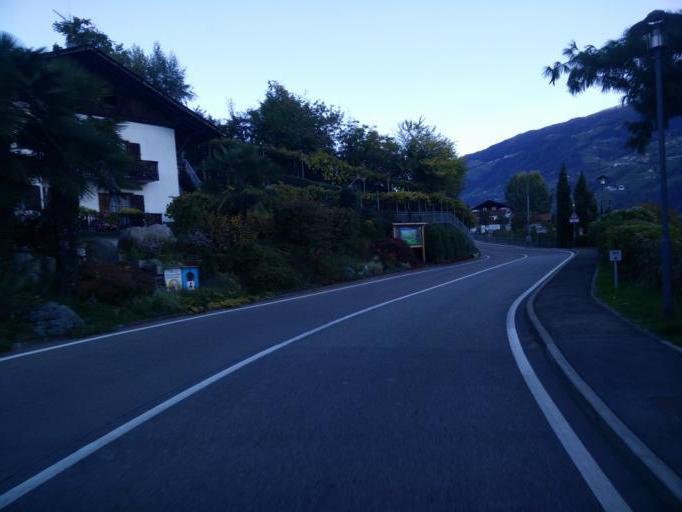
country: IT
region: Trentino-Alto Adige
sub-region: Bolzano
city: Caines
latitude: 46.6979
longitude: 11.1767
